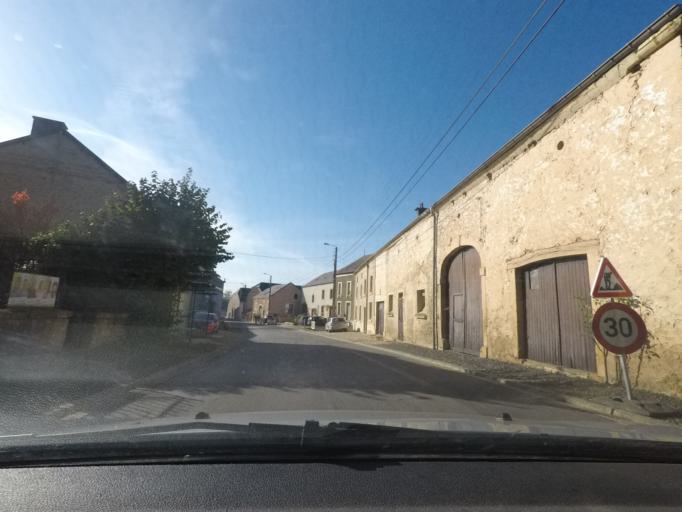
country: BE
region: Wallonia
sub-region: Province du Luxembourg
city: Arlon
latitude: 49.6375
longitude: 5.7715
